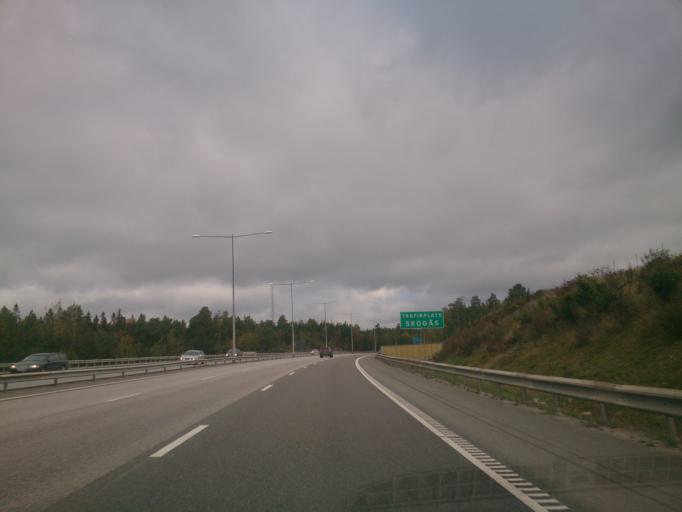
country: SE
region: Stockholm
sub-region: Haninge Kommun
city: Handen
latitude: 59.2090
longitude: 18.1306
